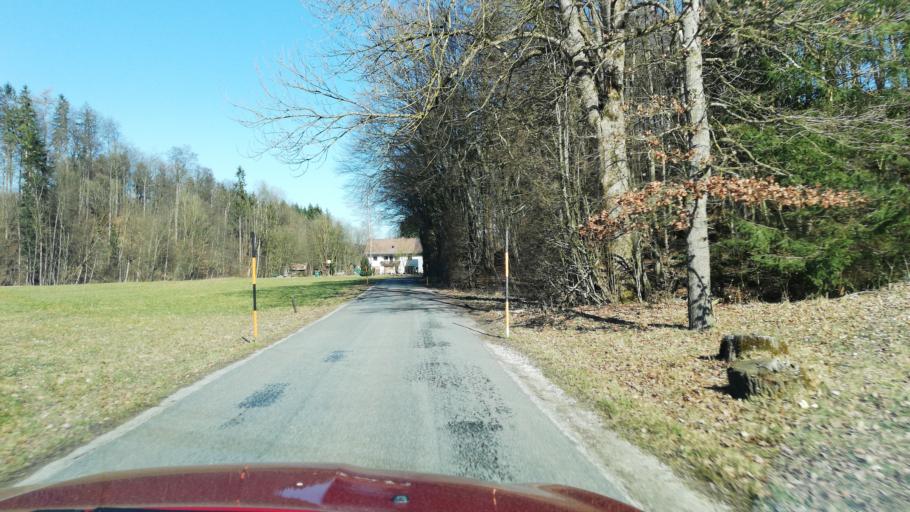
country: AT
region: Upper Austria
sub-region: Politischer Bezirk Vocklabruck
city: Aurach am Hongar
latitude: 47.9704
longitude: 13.6994
